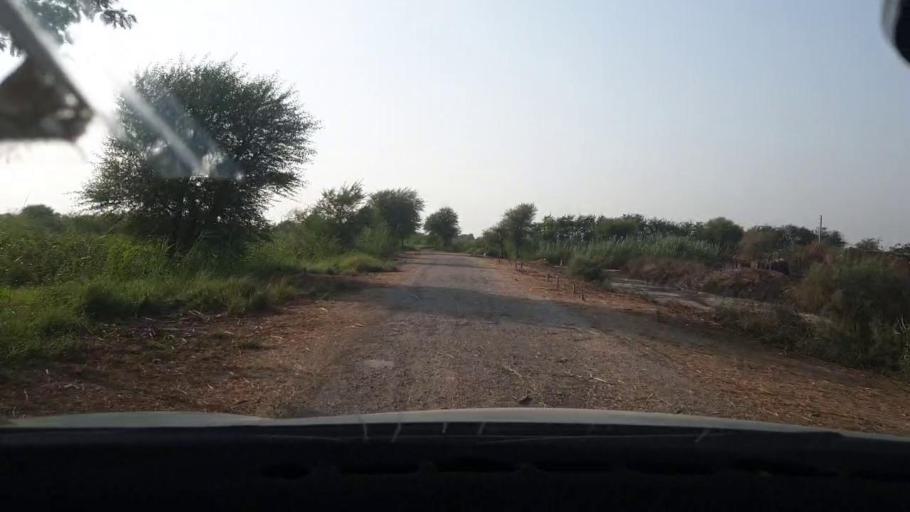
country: PK
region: Sindh
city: Berani
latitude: 25.8163
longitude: 68.7992
